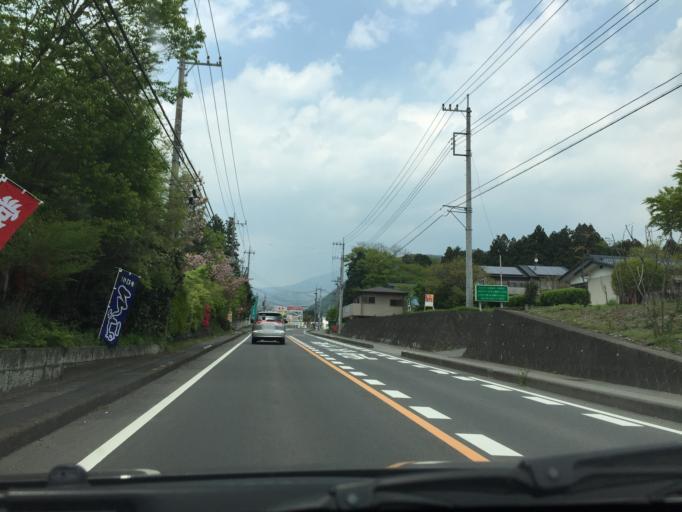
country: JP
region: Tochigi
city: Imaichi
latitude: 36.8110
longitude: 139.7104
